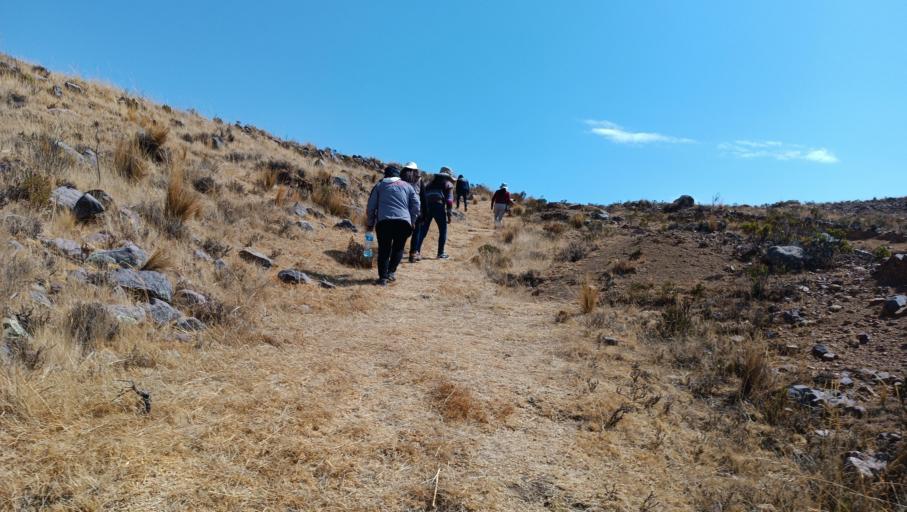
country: BO
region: La Paz
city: Batallas
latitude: -16.3502
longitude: -68.6510
